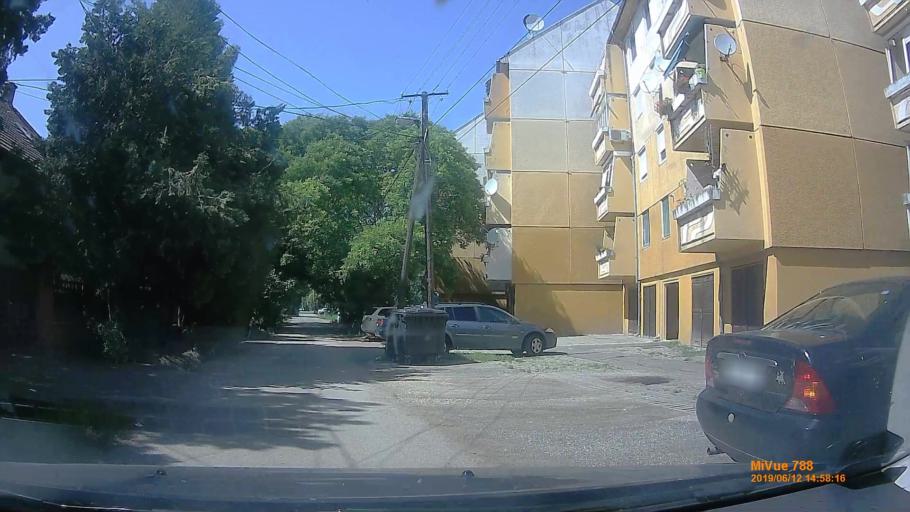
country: HU
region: Csongrad
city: Mako
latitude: 46.2073
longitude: 20.4679
